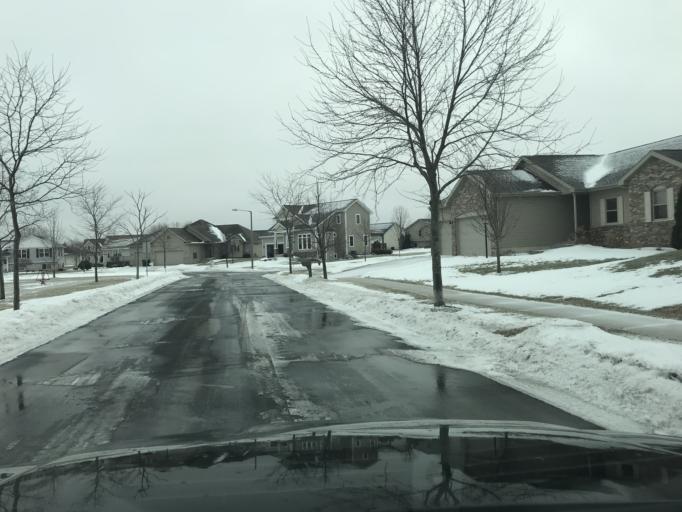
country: US
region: Wisconsin
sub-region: Dane County
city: Cottage Grove
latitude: 43.0931
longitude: -89.2147
